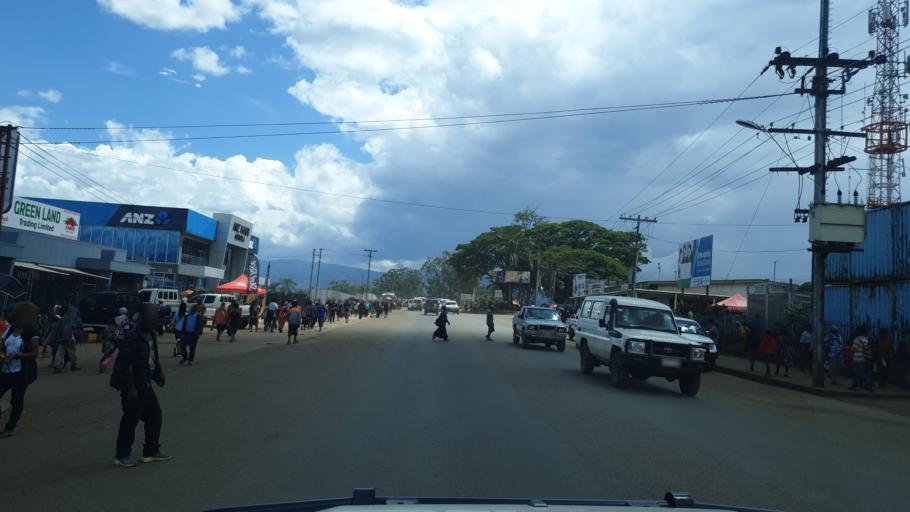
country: PG
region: Eastern Highlands
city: Goroka
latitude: -6.0731
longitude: 145.3930
